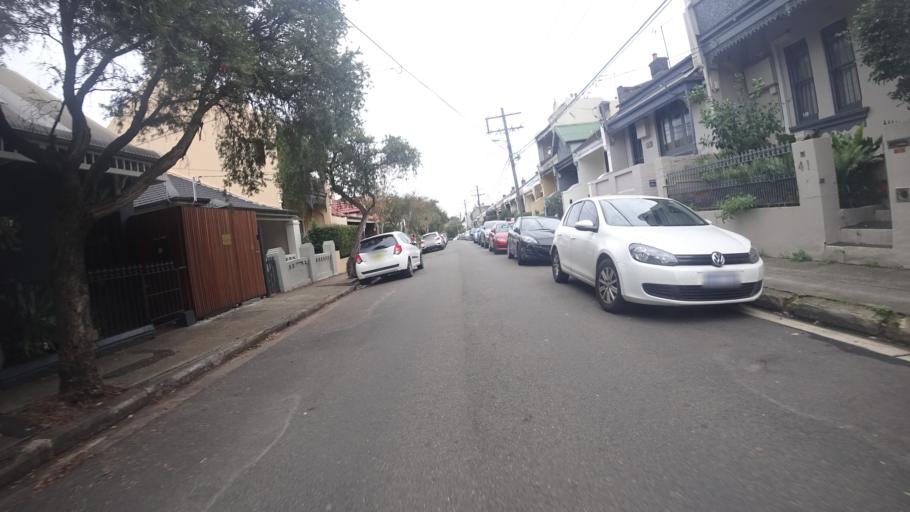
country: AU
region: New South Wales
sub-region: Marrickville
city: Newtown
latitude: -33.9056
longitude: 151.1793
